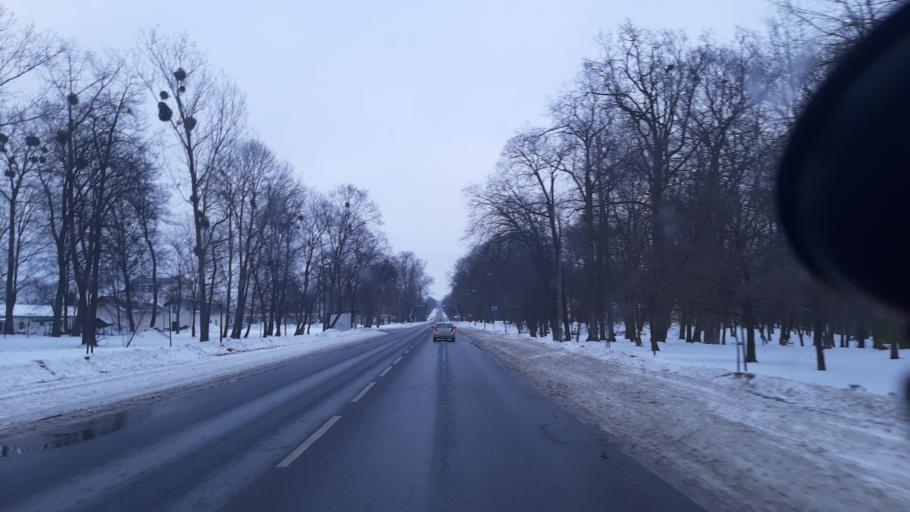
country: PL
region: Lublin Voivodeship
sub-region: Powiat lubelski
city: Garbow
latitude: 51.3548
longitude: 22.3305
